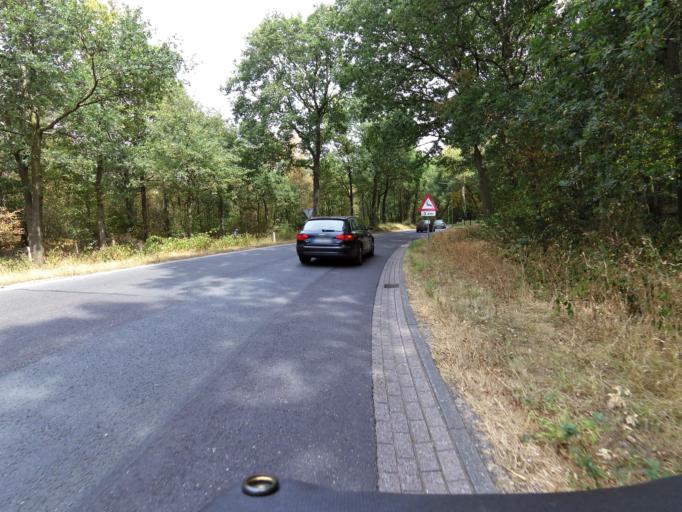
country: NL
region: Limburg
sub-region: Gemeente Bergen
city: Wellerlooi
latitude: 51.5585
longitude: 6.0950
